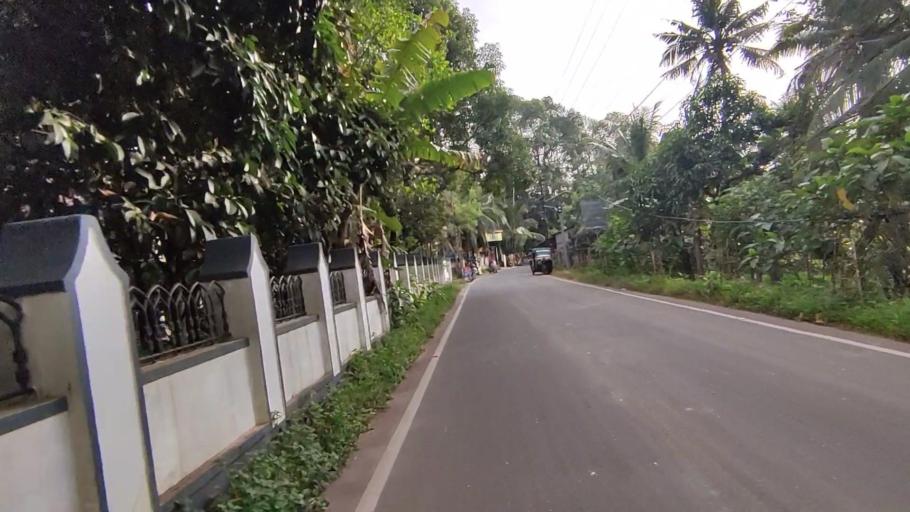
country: IN
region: Kerala
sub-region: Kottayam
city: Kottayam
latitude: 9.6005
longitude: 76.4968
